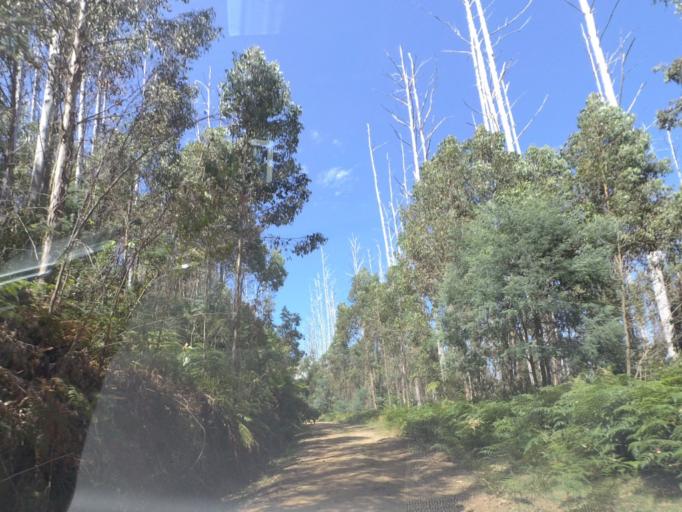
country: AU
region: Victoria
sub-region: Murrindindi
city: Alexandra
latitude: -37.4755
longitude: 145.8301
